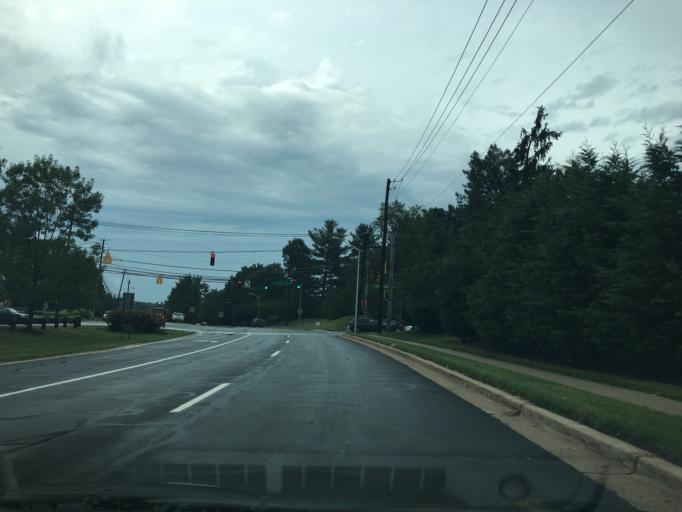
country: US
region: Maryland
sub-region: Montgomery County
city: Gaithersburg
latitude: 39.1146
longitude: -77.2157
